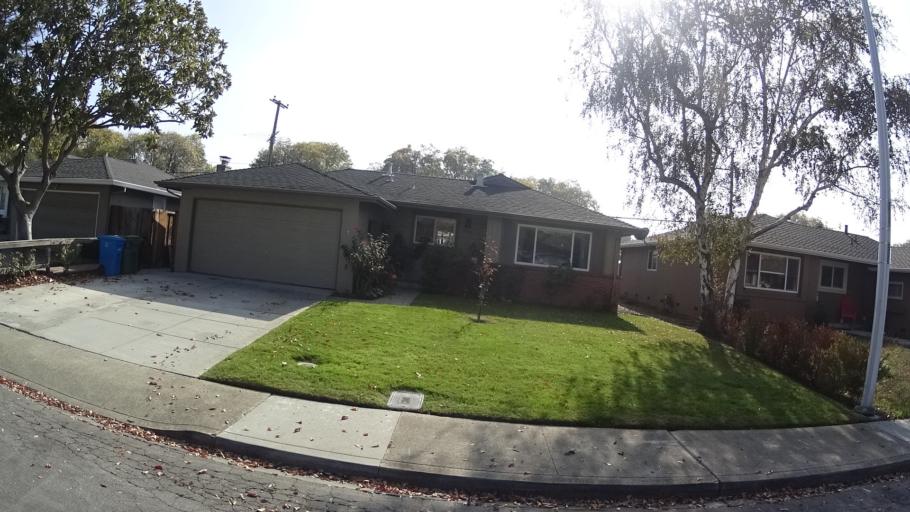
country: US
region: California
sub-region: Santa Clara County
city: Santa Clara
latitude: 37.3606
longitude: -121.9940
